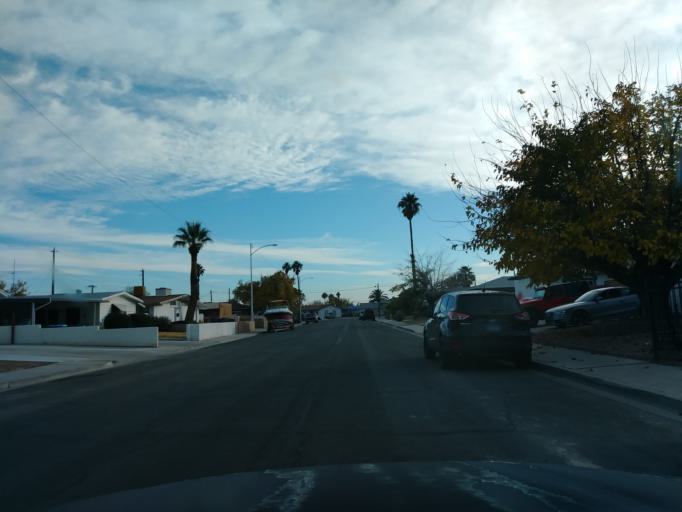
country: US
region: Nevada
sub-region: Clark County
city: Spring Valley
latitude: 36.1711
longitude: -115.2263
